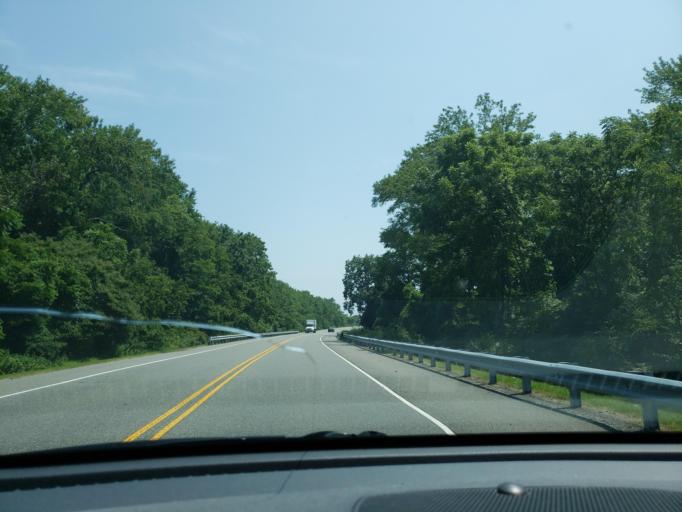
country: US
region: New Jersey
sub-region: Cape May County
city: Erma
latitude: 38.9733
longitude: -74.9322
